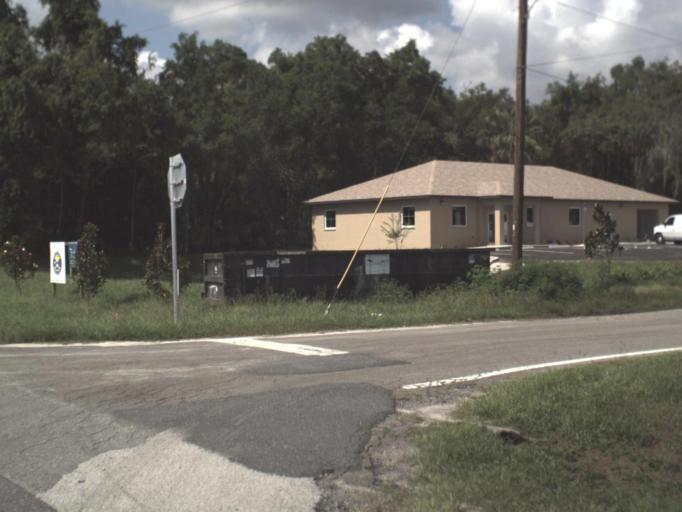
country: US
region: Florida
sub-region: Citrus County
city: Inverness
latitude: 28.8476
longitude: -82.3446
